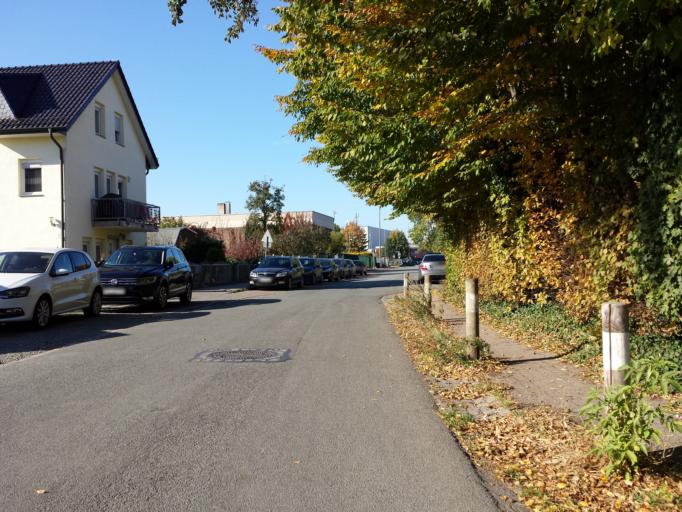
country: DE
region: Lower Saxony
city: Ritterhude
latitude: 53.1389
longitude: 8.7276
